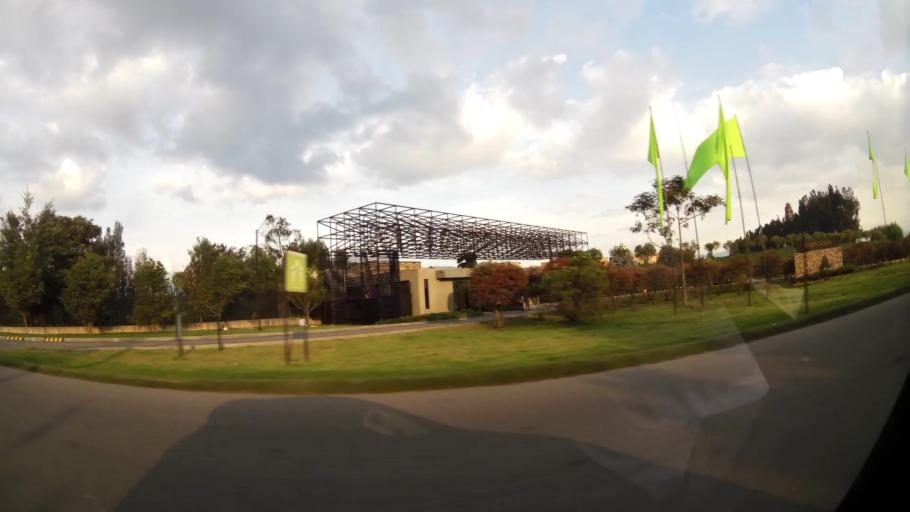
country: CO
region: Cundinamarca
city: Cota
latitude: 4.8162
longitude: -74.0900
